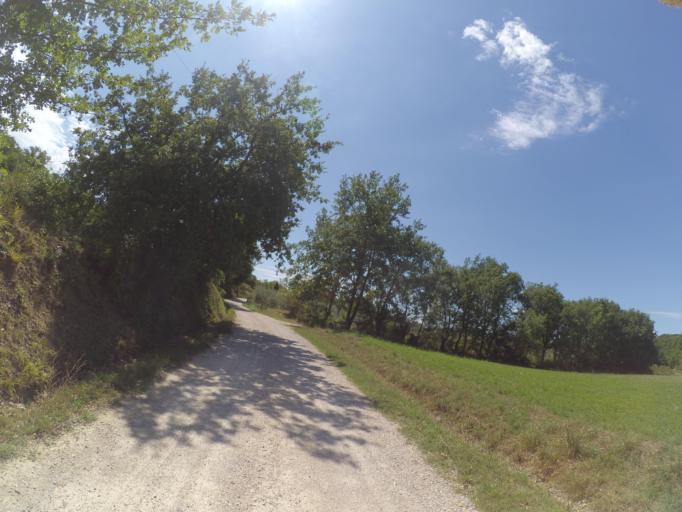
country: IT
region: Tuscany
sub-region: Province of Arezzo
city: Castiglion Fibocchi
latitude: 43.5362
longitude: 11.7661
